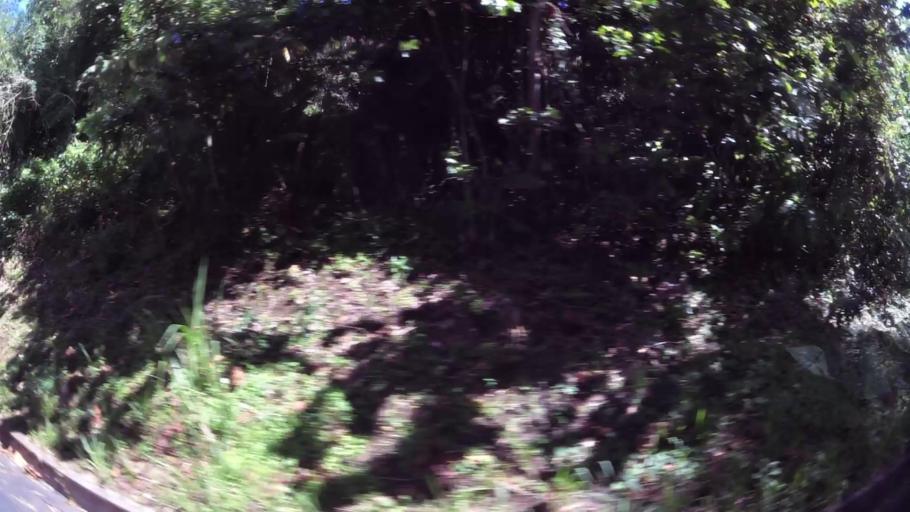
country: DM
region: Saint Paul
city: Pont Casse
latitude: 15.3470
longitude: -61.3666
